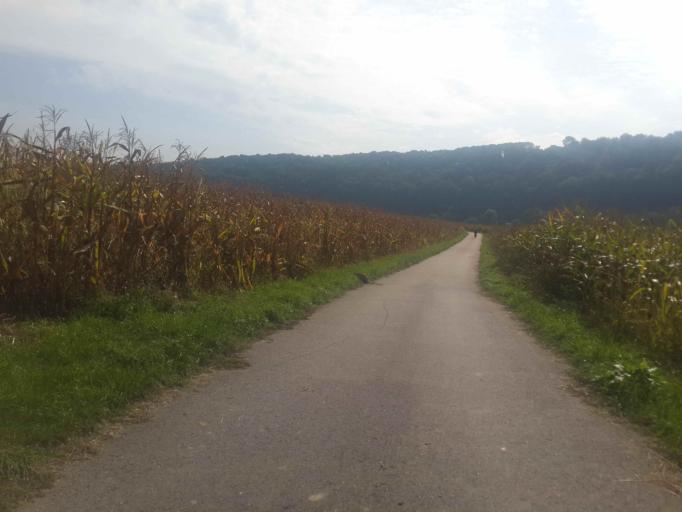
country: DE
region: Baden-Wuerttemberg
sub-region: Regierungsbezirk Stuttgart
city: Neudenau
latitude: 49.2895
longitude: 9.2849
